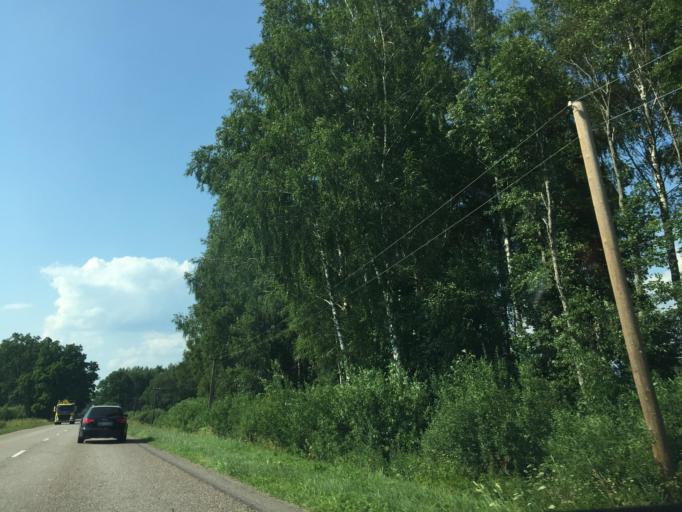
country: LV
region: Limbazu Rajons
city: Limbazi
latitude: 57.4881
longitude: 24.8566
